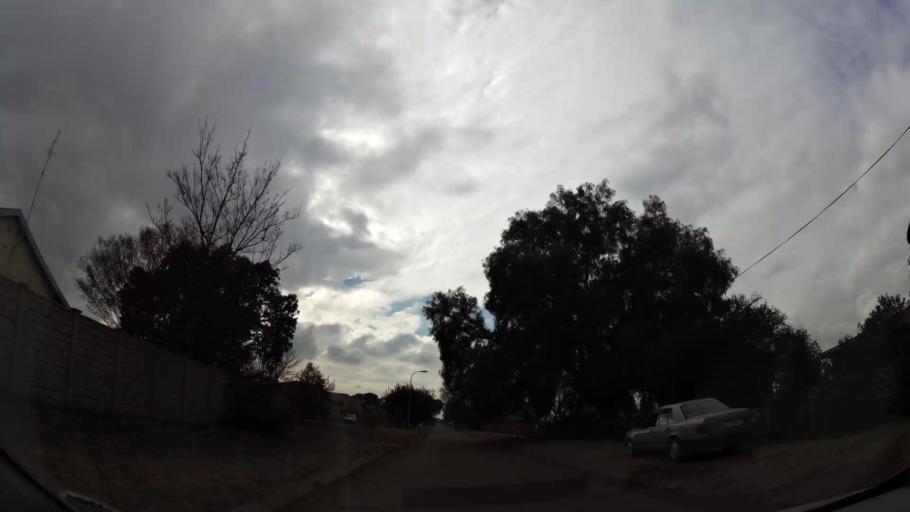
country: ZA
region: Gauteng
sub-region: Sedibeng District Municipality
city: Meyerton
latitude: -26.5900
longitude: 27.9945
